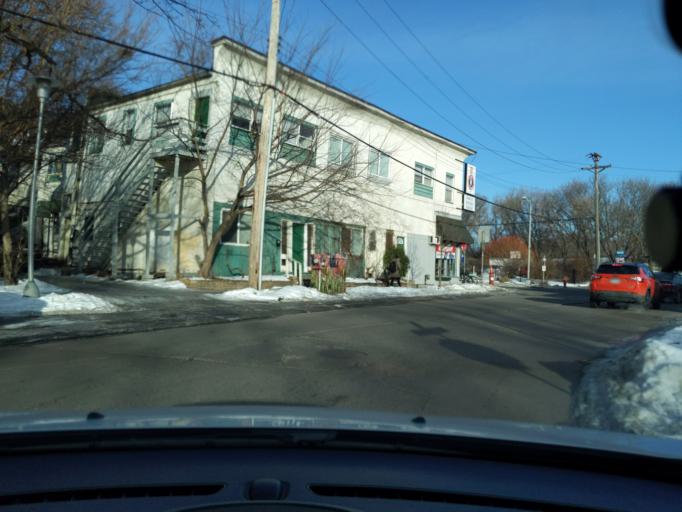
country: US
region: Minnesota
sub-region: Ramsey County
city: Lauderdale
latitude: 44.9875
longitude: -93.2215
